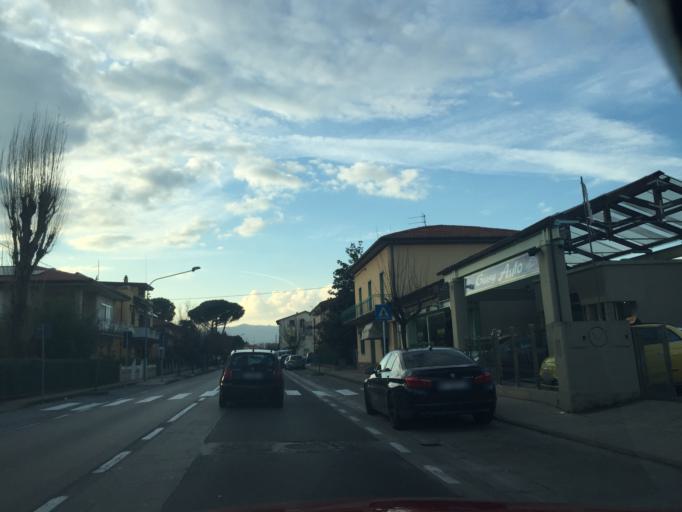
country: IT
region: Tuscany
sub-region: Provincia di Pistoia
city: Pieve a Nievole
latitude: 43.8737
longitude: 10.8042
